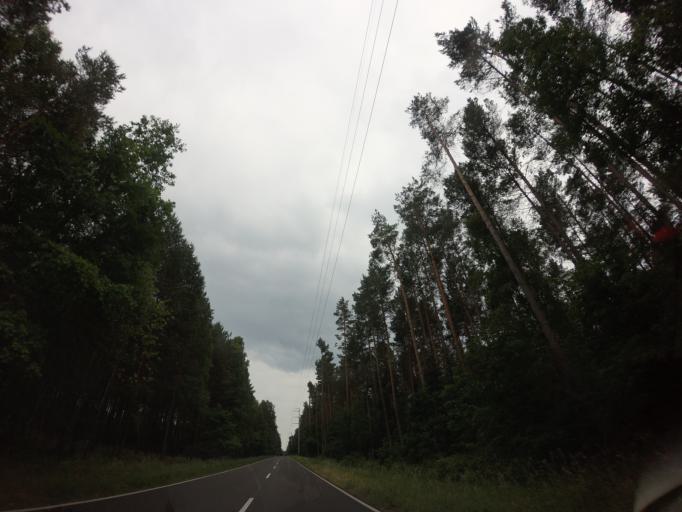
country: PL
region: West Pomeranian Voivodeship
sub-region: Powiat drawski
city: Czaplinek
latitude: 53.4979
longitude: 16.2234
